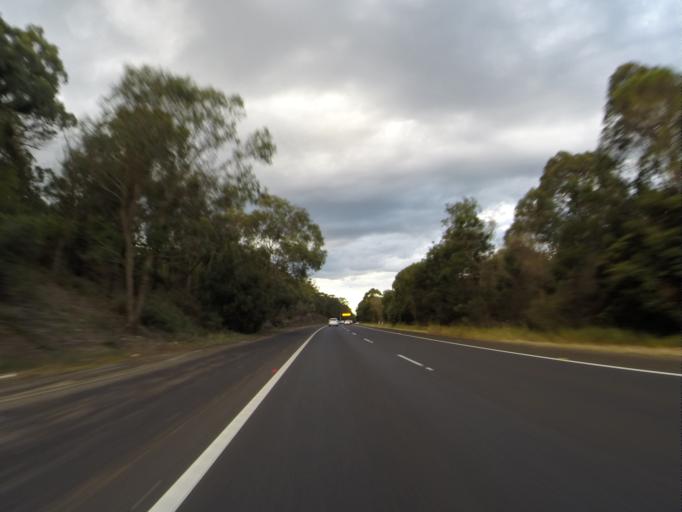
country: AU
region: New South Wales
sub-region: Wollondilly
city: Buxton
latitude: -34.2984
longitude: 150.6130
